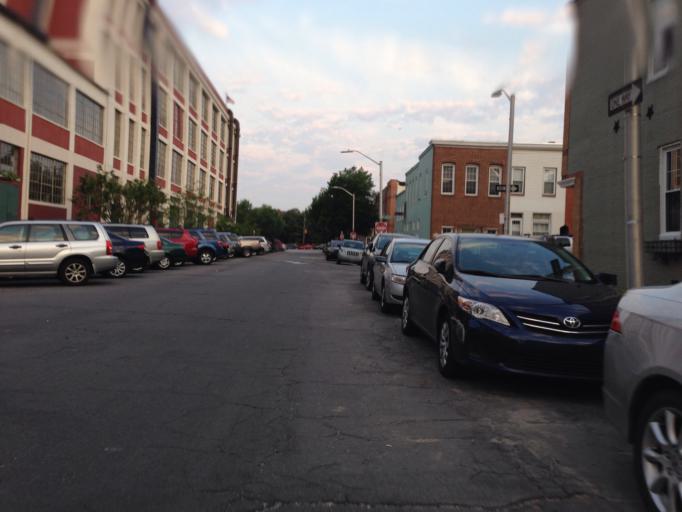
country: US
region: Maryland
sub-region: City of Baltimore
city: Baltimore
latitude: 39.2821
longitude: -76.5808
